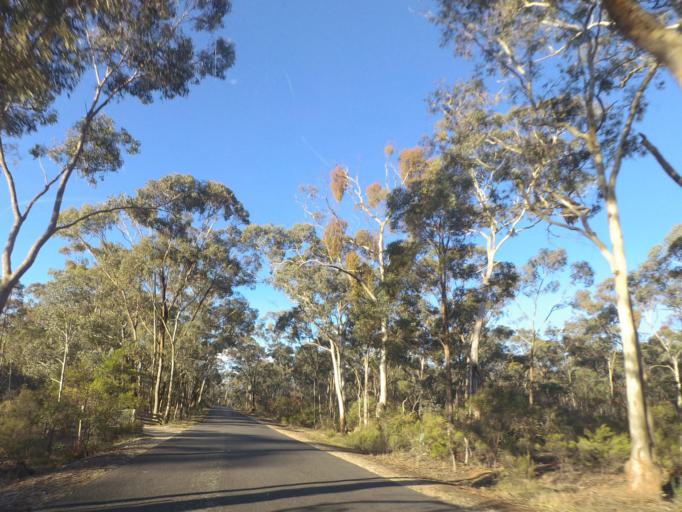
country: AU
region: Victoria
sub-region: Mount Alexander
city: Castlemaine
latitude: -37.1423
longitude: 144.1973
